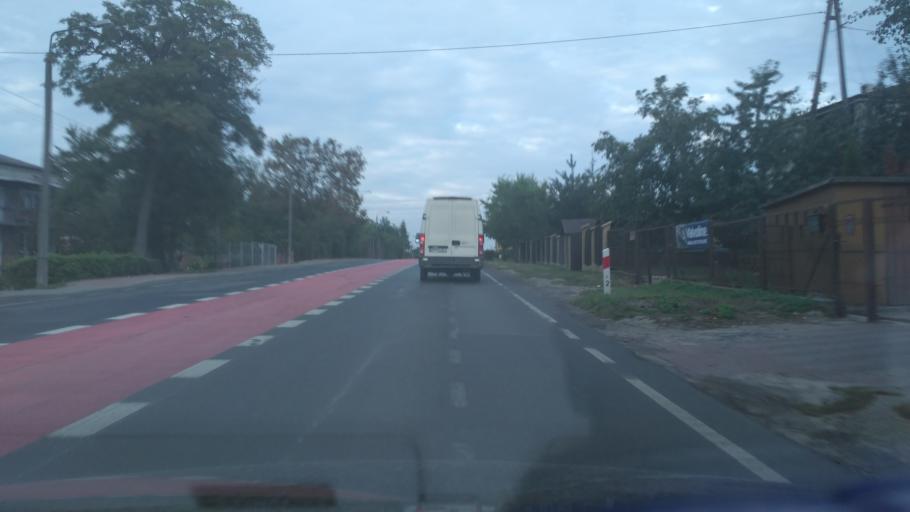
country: PL
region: Lublin Voivodeship
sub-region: Powiat lubelski
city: Jakubowice Murowane
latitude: 51.2675
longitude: 22.6365
